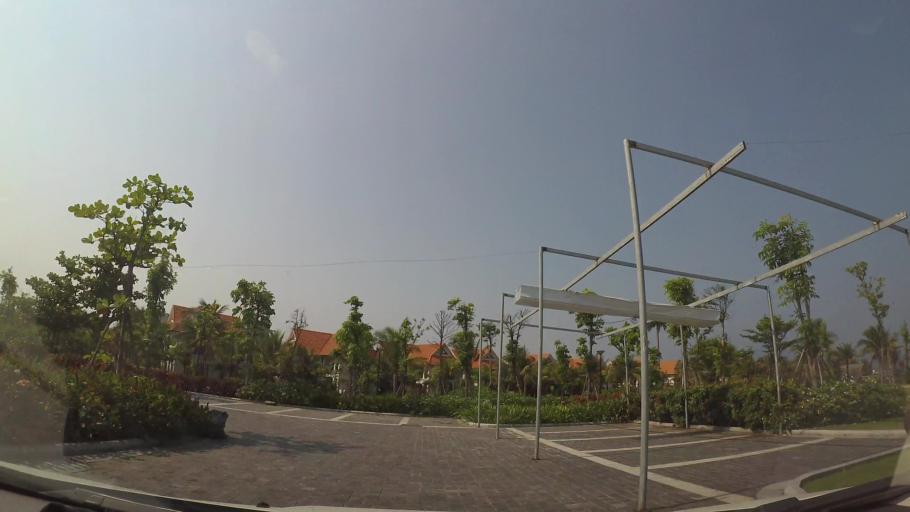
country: VN
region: Da Nang
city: Ngu Hanh Son
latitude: 16.0351
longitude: 108.2532
